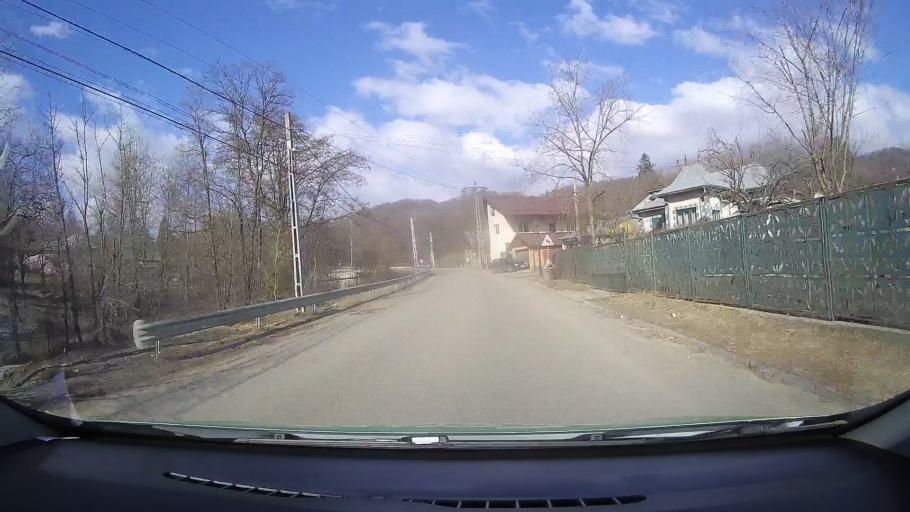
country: RO
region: Dambovita
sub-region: Comuna Varfuri
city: Varfuri
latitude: 45.0901
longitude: 25.4916
